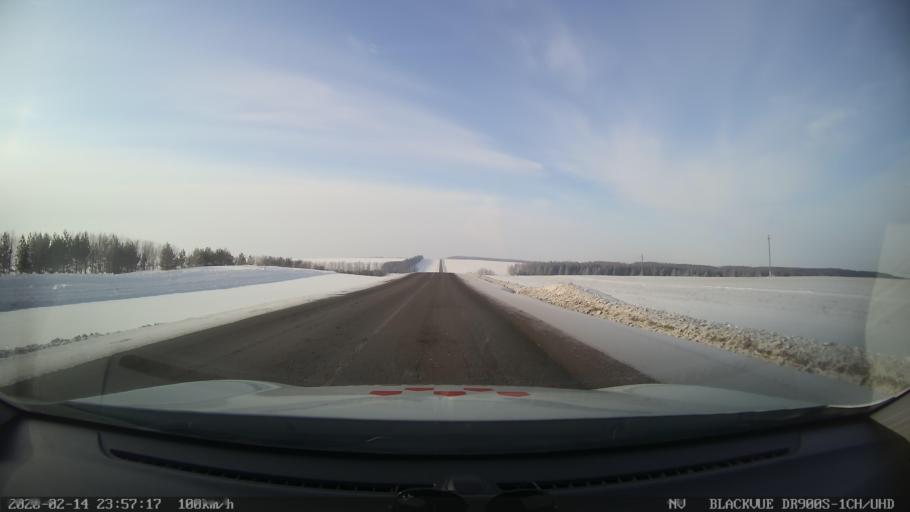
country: RU
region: Tatarstan
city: Kuybyshevskiy Zaton
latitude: 55.3326
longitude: 49.1134
